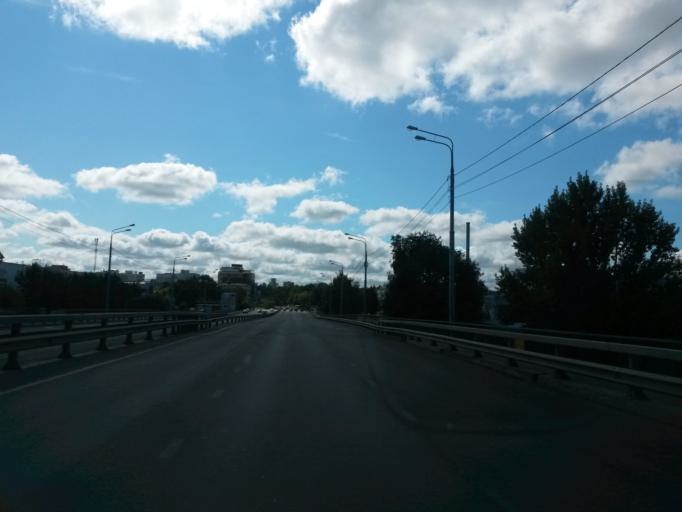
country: RU
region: Jaroslavl
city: Yaroslavl
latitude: 57.6119
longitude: 39.8597
